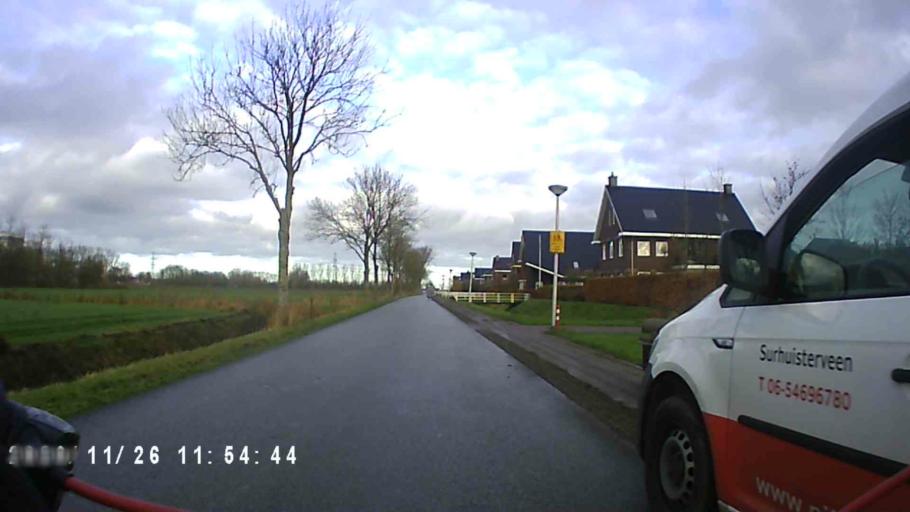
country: NL
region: Groningen
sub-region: Gemeente Bedum
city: Bedum
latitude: 53.3053
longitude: 6.6050
